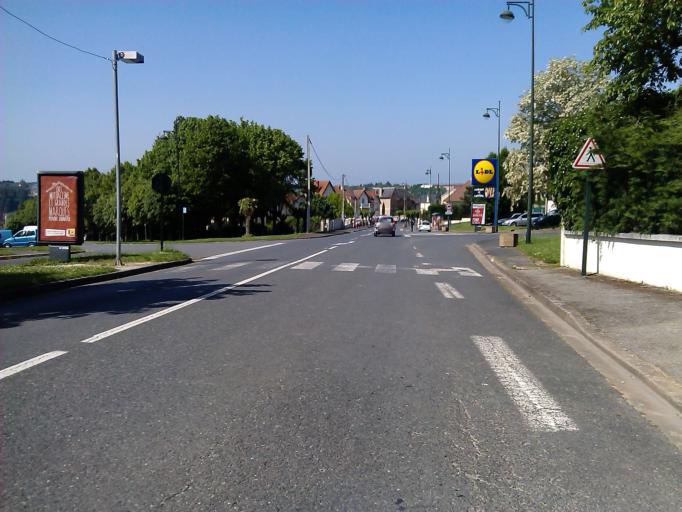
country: FR
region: Centre
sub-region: Departement de l'Indre
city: Argenton-sur-Creuse
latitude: 46.5901
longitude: 1.5308
